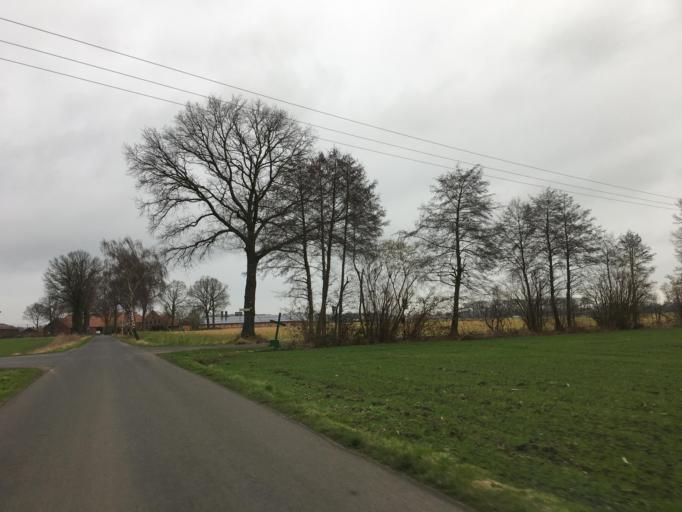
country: DE
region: North Rhine-Westphalia
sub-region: Regierungsbezirk Munster
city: Senden
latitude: 51.8718
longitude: 7.4422
